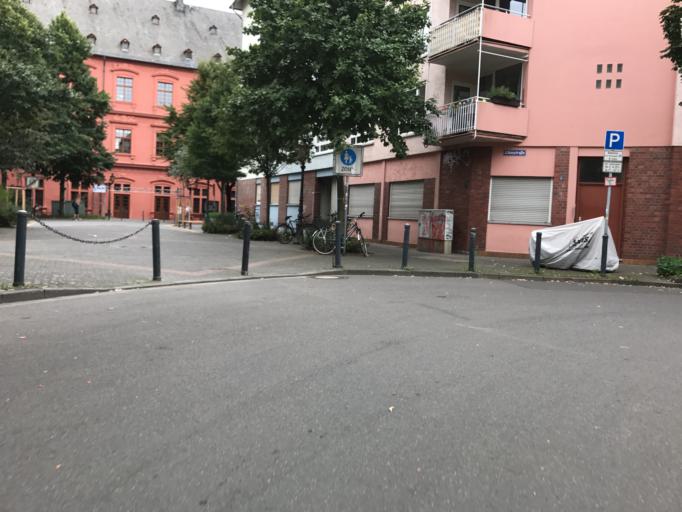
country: DE
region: Rheinland-Pfalz
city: Mainz
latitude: 50.0075
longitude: 8.2692
